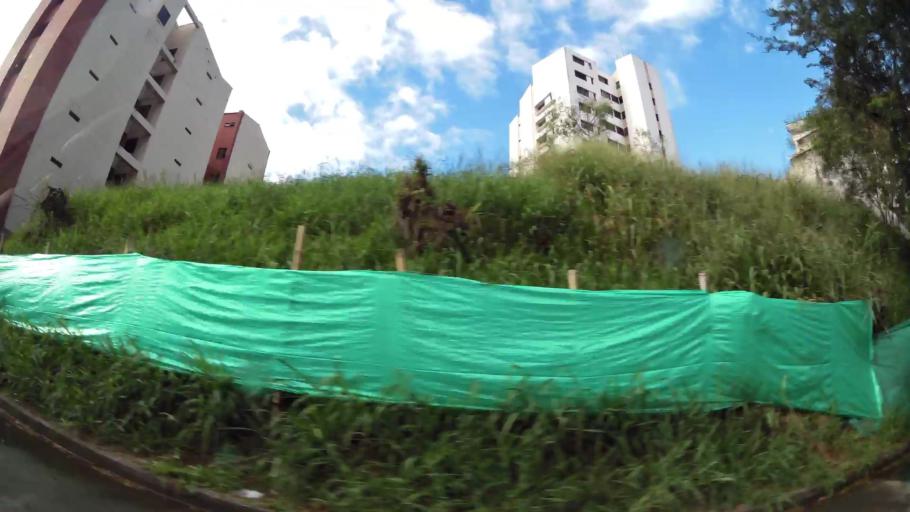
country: CO
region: Valle del Cauca
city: Cali
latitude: 3.4424
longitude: -76.5467
